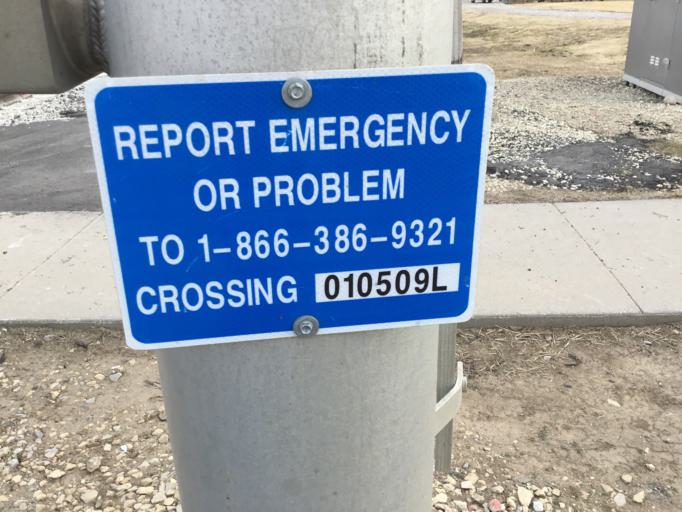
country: US
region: Kansas
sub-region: McPherson County
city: McPherson
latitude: 38.3724
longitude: -97.6852
